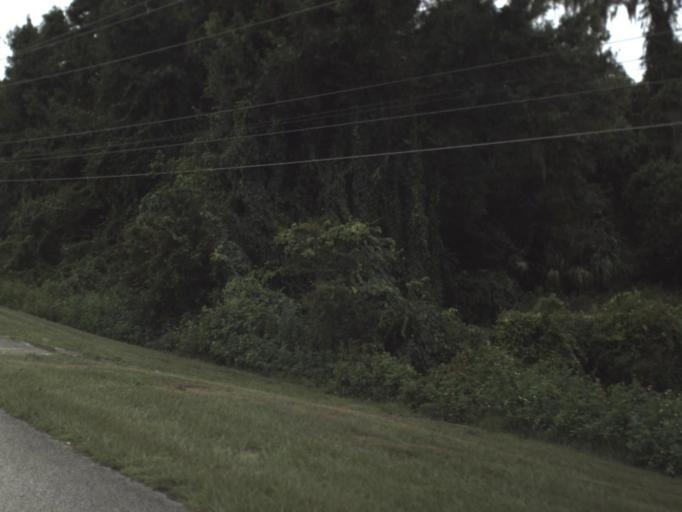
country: US
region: Florida
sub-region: Polk County
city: Bartow
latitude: 27.9083
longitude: -81.8290
